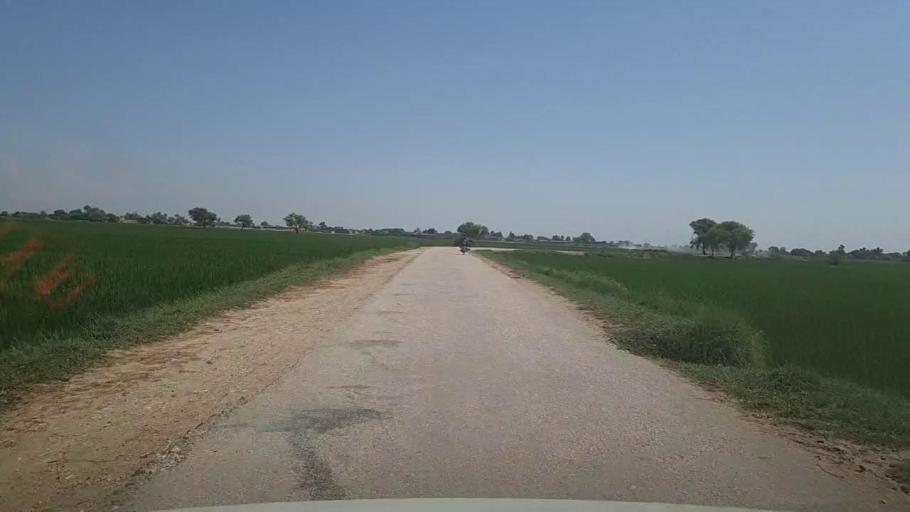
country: PK
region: Sindh
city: Kashmor
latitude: 28.2947
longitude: 69.4339
